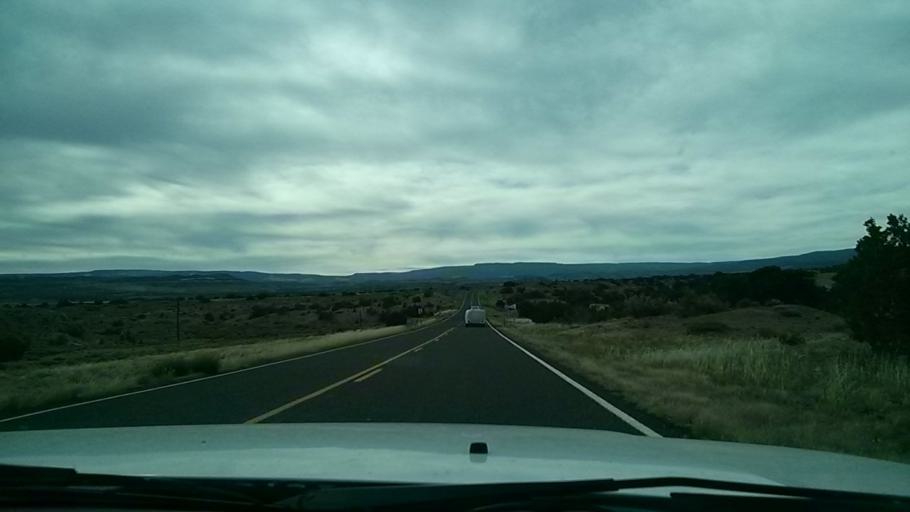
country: US
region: Utah
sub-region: Wayne County
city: Loa
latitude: 37.7392
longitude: -111.5508
